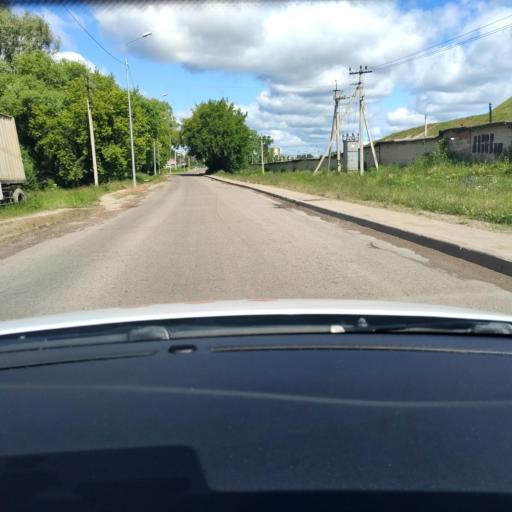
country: RU
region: Tatarstan
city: Vysokaya Gora
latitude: 55.8575
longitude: 49.2443
